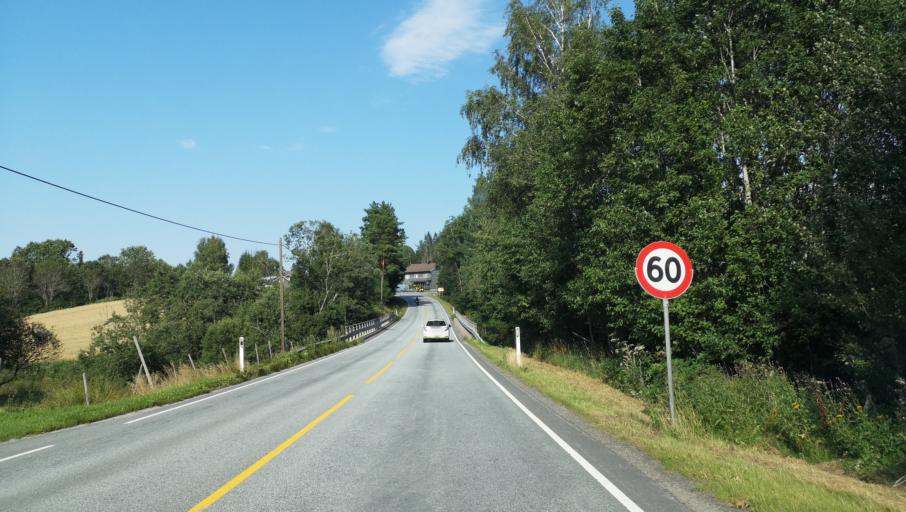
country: NO
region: Ostfold
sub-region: Valer
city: Kirkebygda
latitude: 59.4957
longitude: 10.8374
